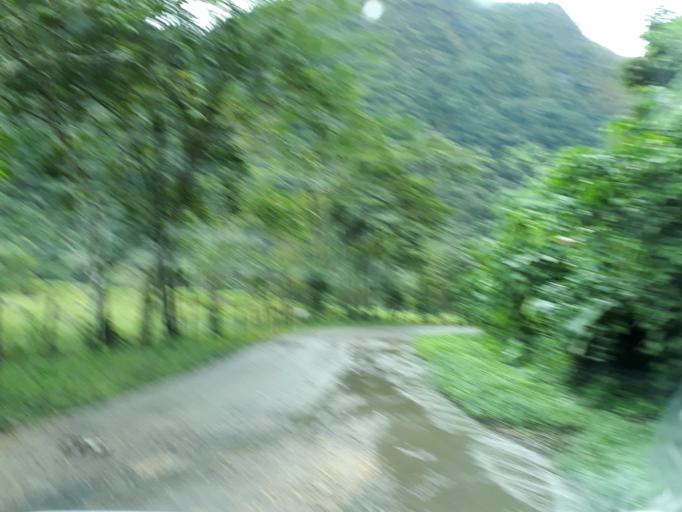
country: CO
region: Boyaca
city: Santa Maria
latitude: 4.7472
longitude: -73.3077
